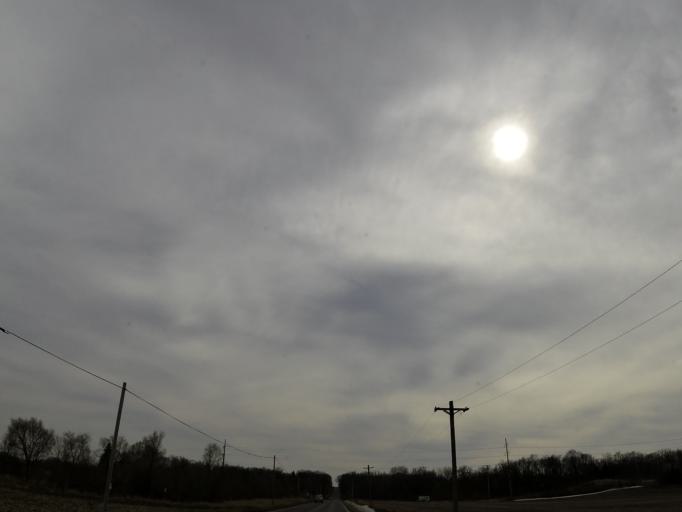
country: US
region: Minnesota
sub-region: Dakota County
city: Rosemount
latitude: 44.7488
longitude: -93.0547
